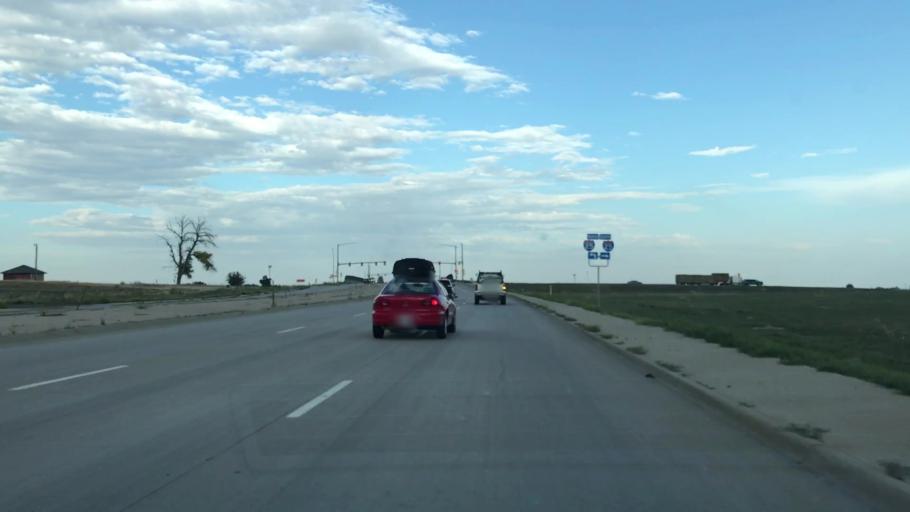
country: US
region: Colorado
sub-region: Weld County
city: Mead
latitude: 40.2040
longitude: -104.9843
